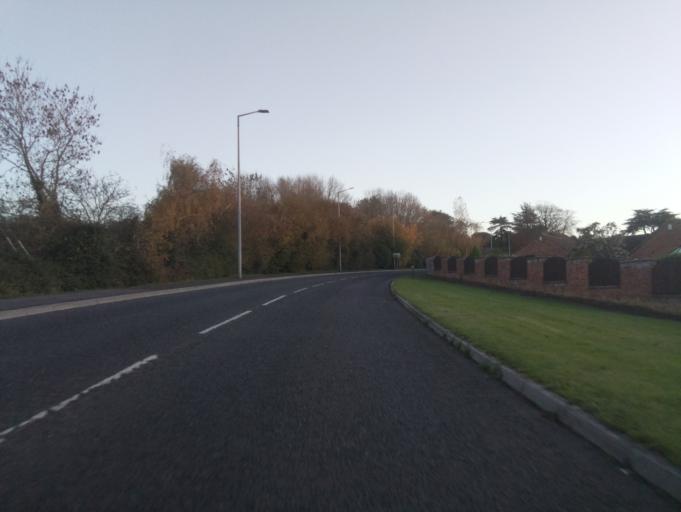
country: GB
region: England
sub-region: Wiltshire
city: Westbury
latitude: 51.2644
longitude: -2.1731
